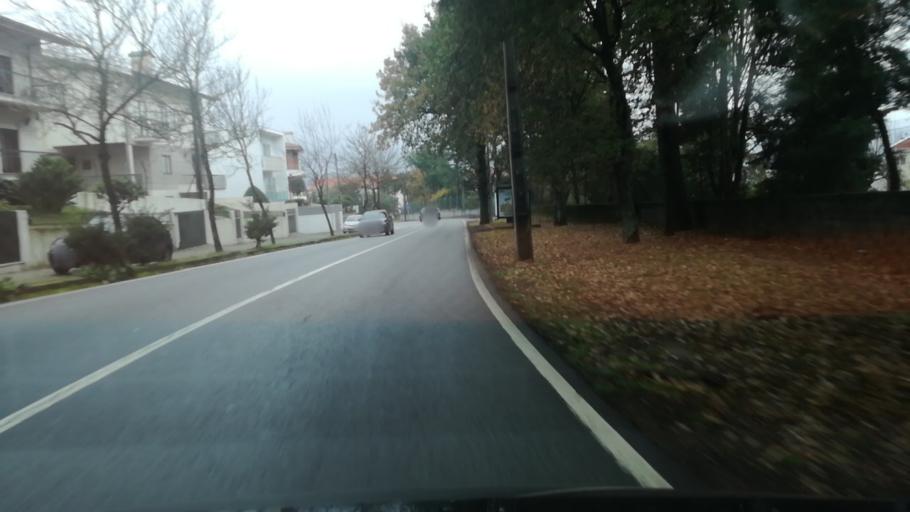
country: PT
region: Braga
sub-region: Braga
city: Braga
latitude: 41.5343
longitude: -8.4042
